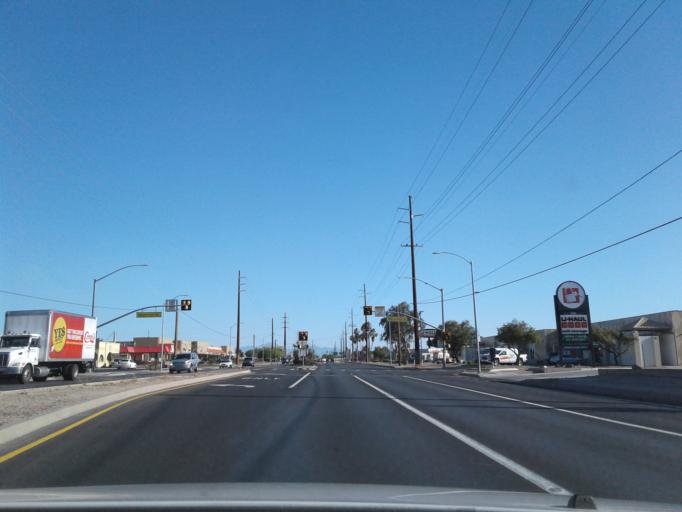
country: US
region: Arizona
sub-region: Pima County
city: Tucson
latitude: 32.2035
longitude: -110.9096
